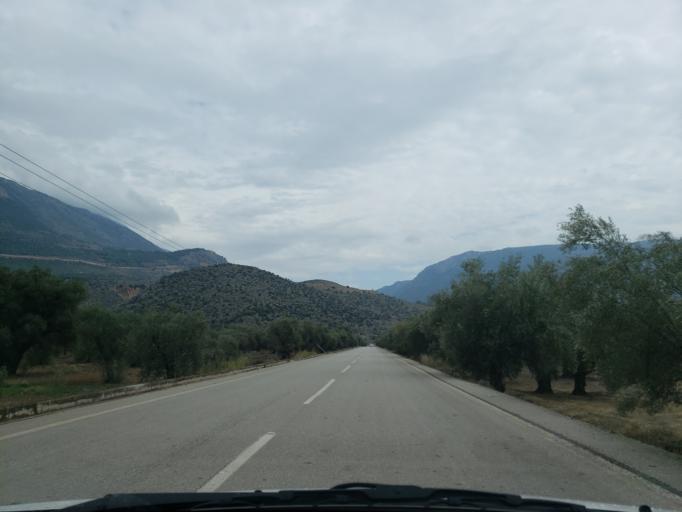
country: GR
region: Central Greece
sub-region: Nomos Fokidos
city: Kirra
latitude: 38.4789
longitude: 22.4447
